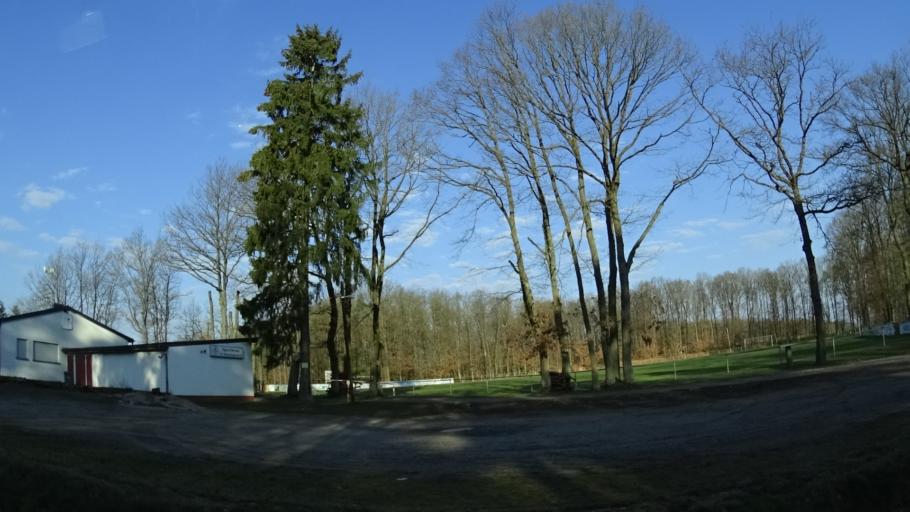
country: DE
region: Rheinland-Pfalz
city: Dickesbach
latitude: 49.7194
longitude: 7.4296
